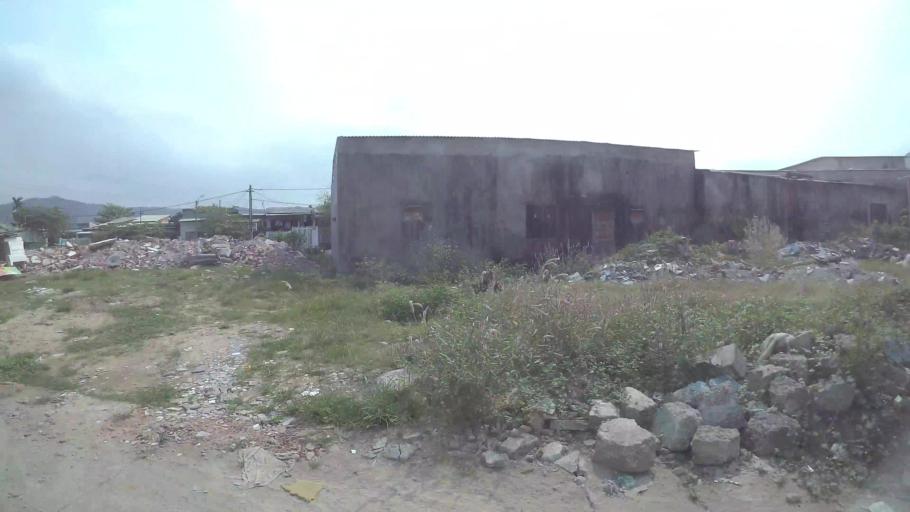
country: VN
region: Da Nang
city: Lien Chieu
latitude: 16.0604
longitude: 108.1587
